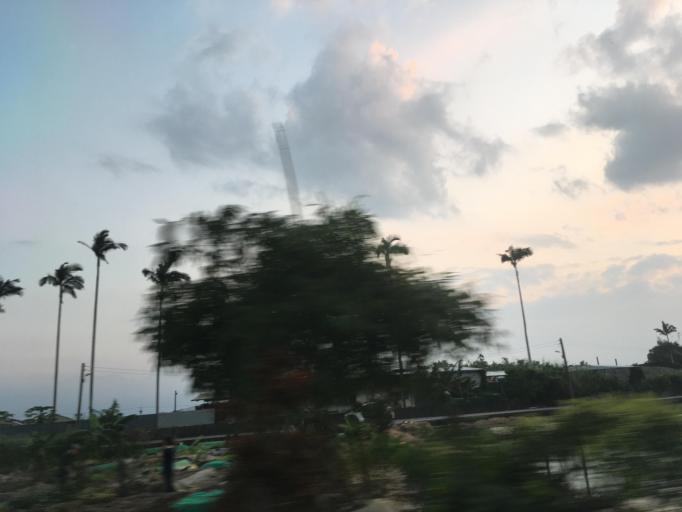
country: TW
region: Taiwan
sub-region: Yilan
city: Yilan
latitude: 24.6907
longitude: 121.7854
